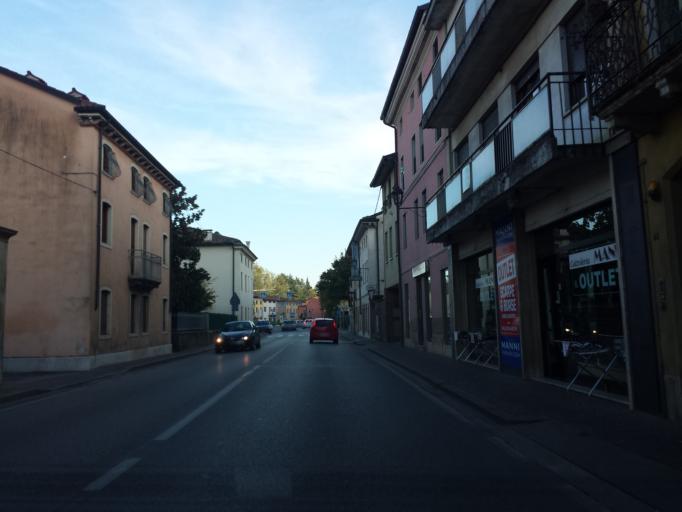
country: IT
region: Veneto
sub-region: Provincia di Vicenza
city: Isola Vicentina
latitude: 45.6283
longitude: 11.4440
